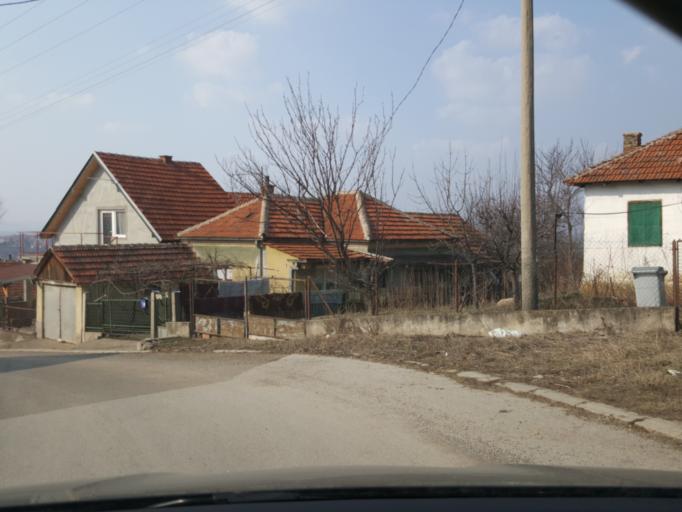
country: RS
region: Central Serbia
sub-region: Nisavski Okrug
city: Aleksinac
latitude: 43.5363
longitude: 21.7196
